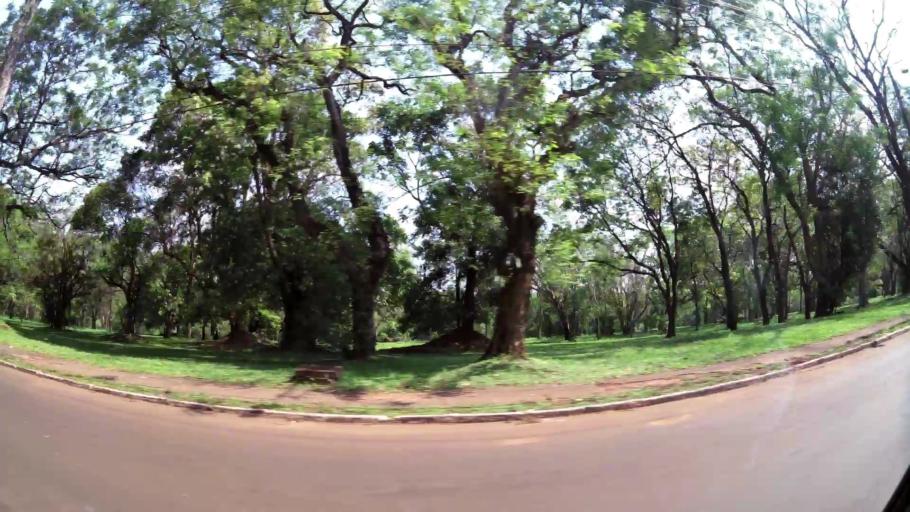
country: PY
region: Alto Parana
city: Ciudad del Este
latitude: -25.5140
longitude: -54.6272
